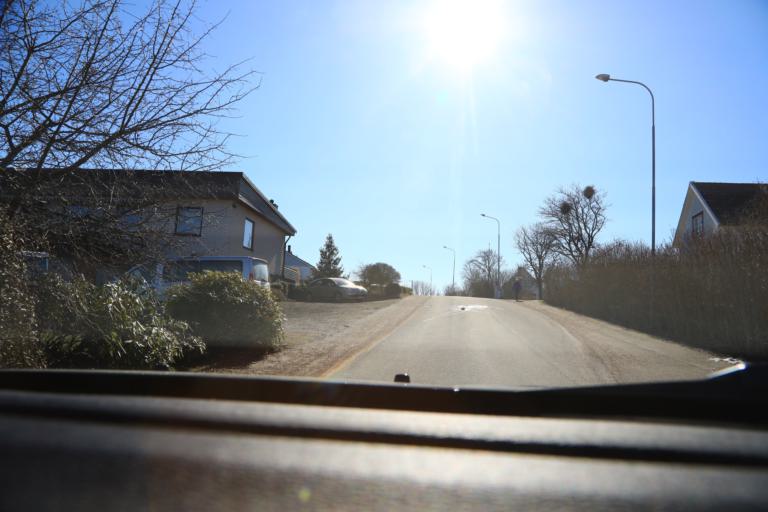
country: SE
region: Halland
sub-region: Kungsbacka Kommun
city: Frillesas
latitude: 57.2322
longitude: 12.1229
